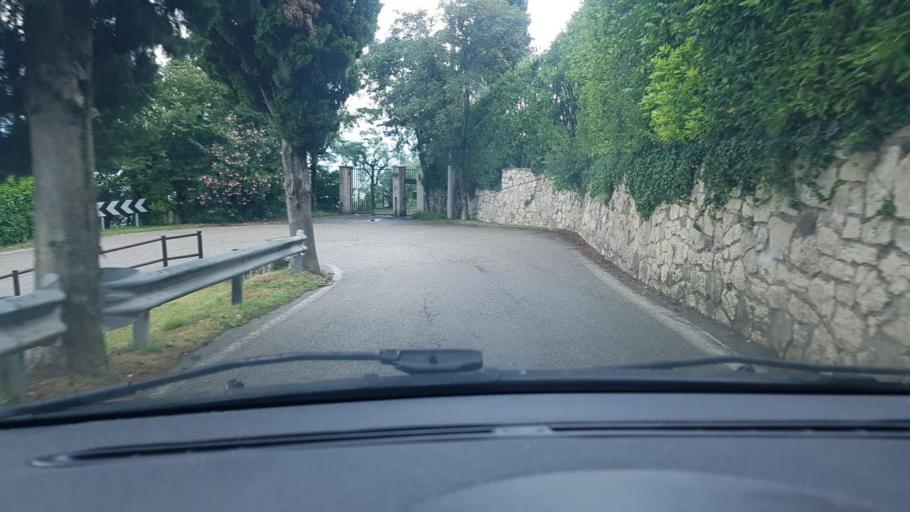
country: IT
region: Veneto
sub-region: Provincia di Verona
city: Torri del Benaco
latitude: 45.6088
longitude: 10.7002
